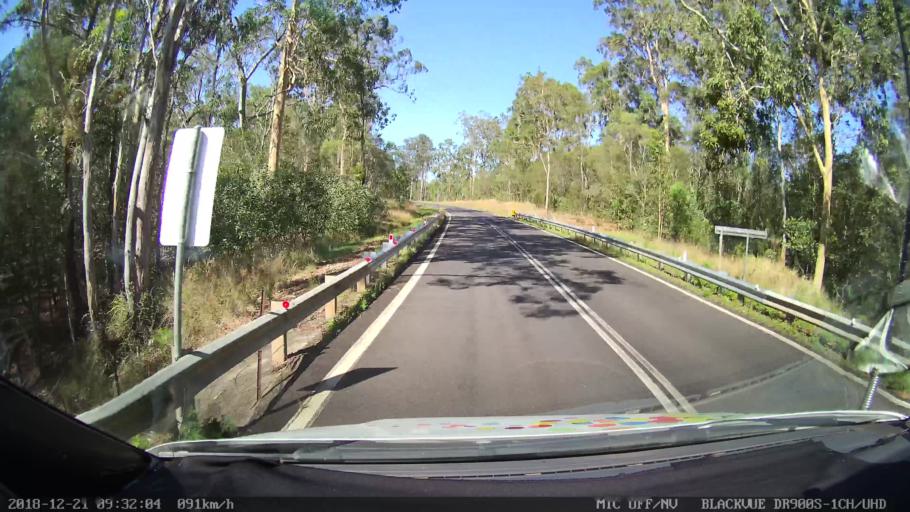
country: AU
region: New South Wales
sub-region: Clarence Valley
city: Maclean
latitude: -29.4661
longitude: 152.9814
